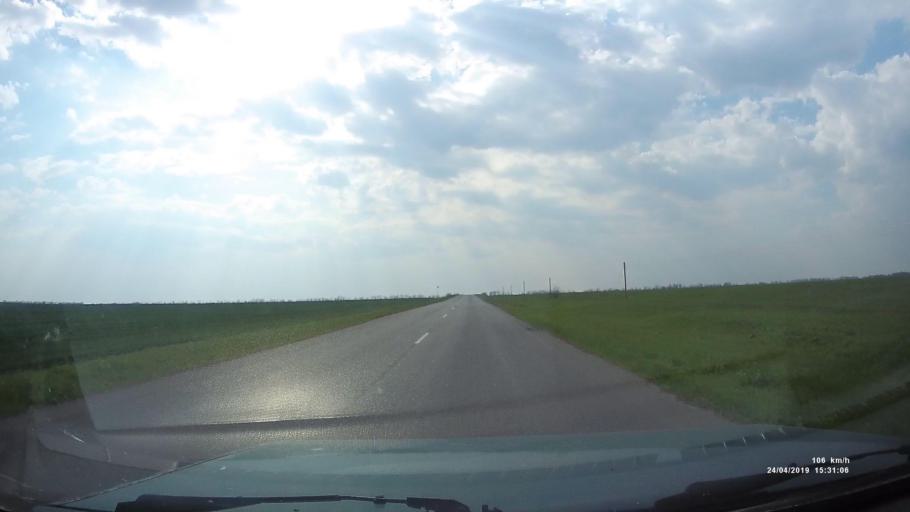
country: RU
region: Rostov
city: Remontnoye
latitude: 46.5998
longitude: 42.9909
